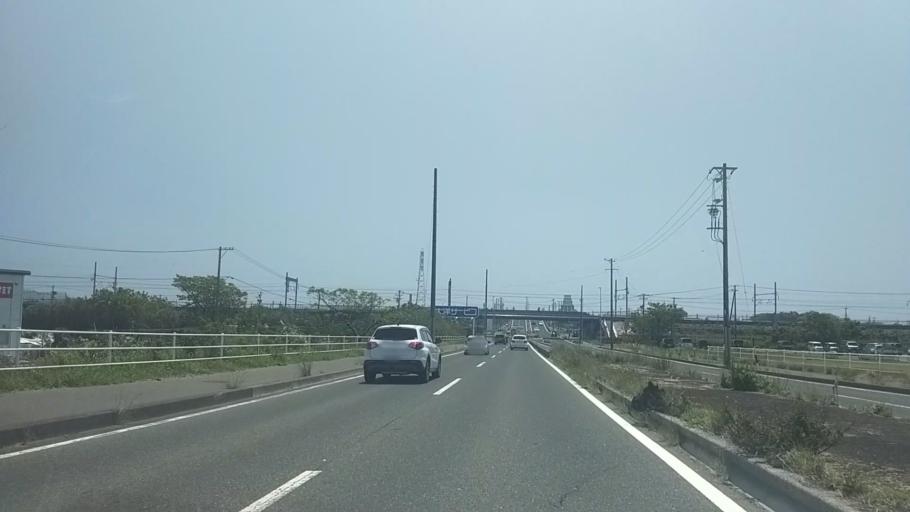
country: JP
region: Shizuoka
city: Hamamatsu
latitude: 34.6899
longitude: 137.6474
